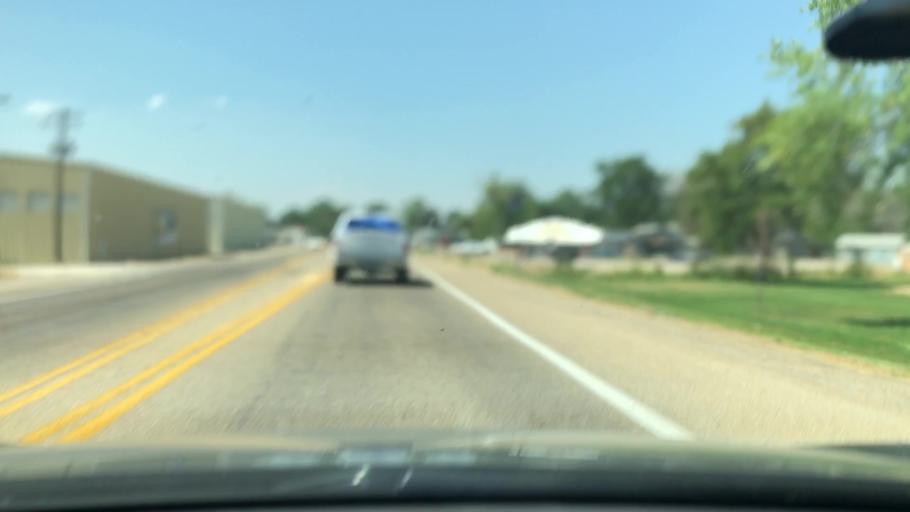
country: US
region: Idaho
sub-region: Canyon County
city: Parma
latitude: 43.7804
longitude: -116.9346
